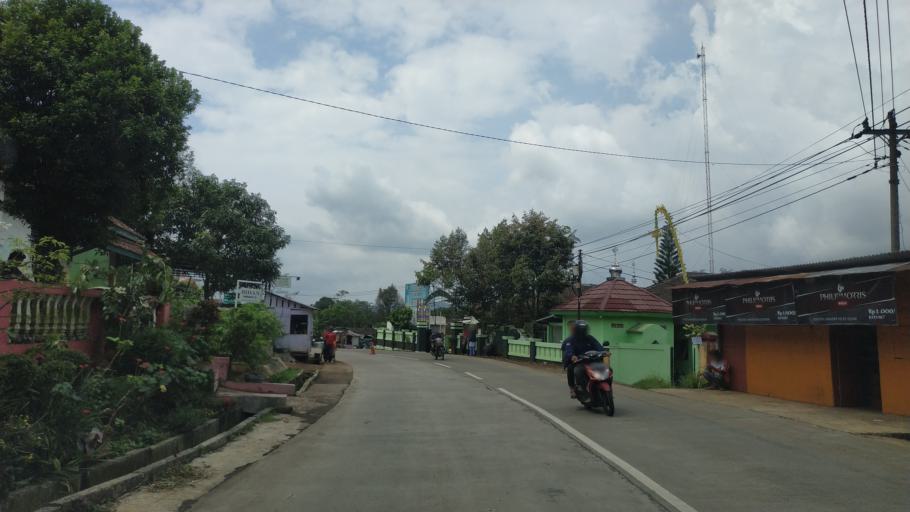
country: ID
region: Central Java
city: Weleri
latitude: -7.1057
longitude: 110.0763
